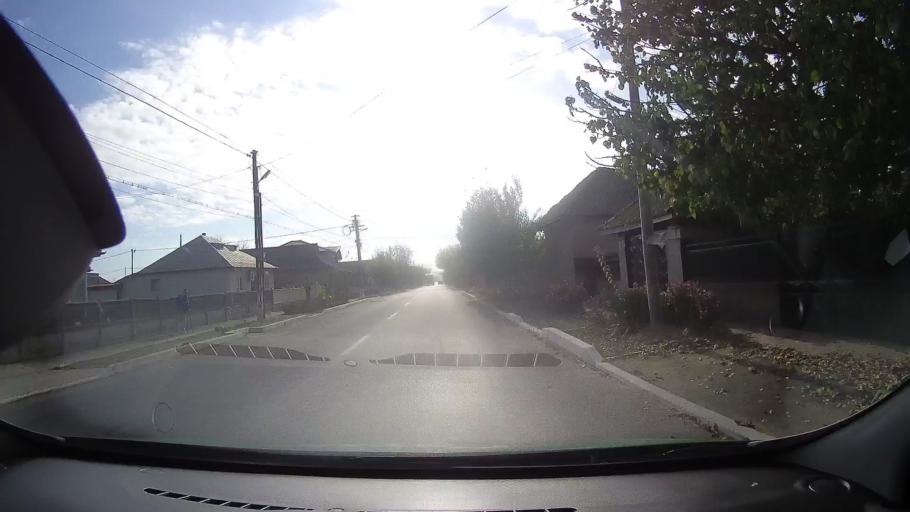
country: RO
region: Tulcea
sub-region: Comuna Sarichioi
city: Sarichioi
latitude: 44.9478
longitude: 28.8524
